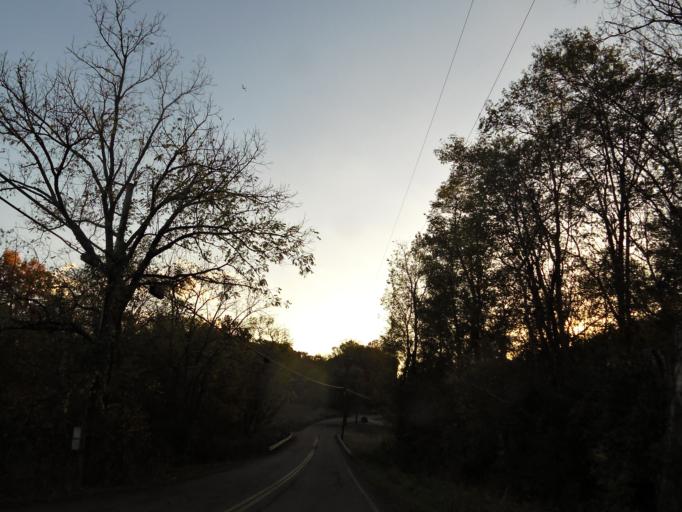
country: US
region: Tennessee
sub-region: Sevier County
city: Seymour
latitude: 35.9343
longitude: -83.7327
